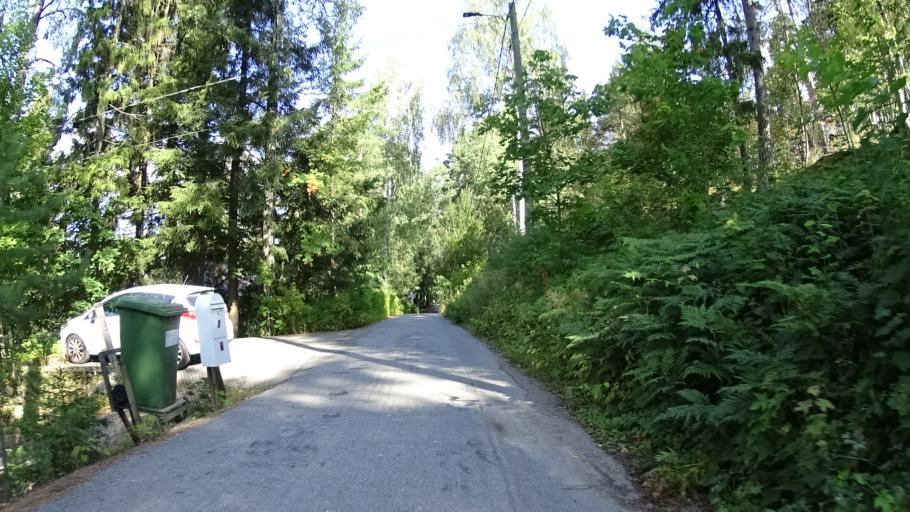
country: FI
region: Uusimaa
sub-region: Helsinki
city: Espoo
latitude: 60.1801
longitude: 24.5921
